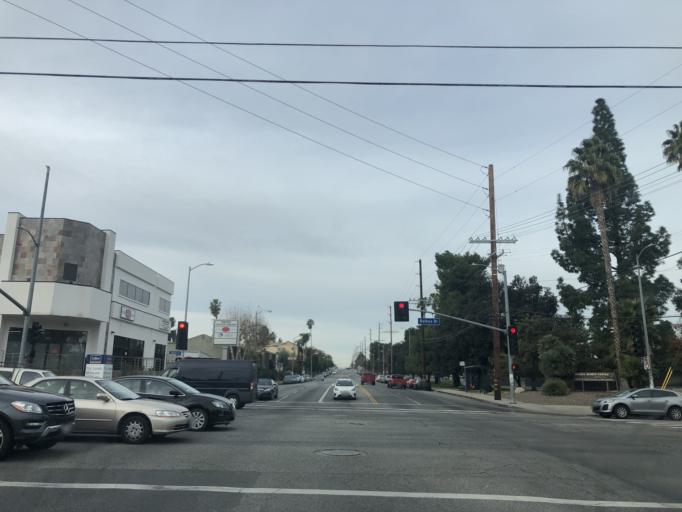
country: US
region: California
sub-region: Los Angeles County
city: Van Nuys
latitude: 34.1722
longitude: -118.5009
